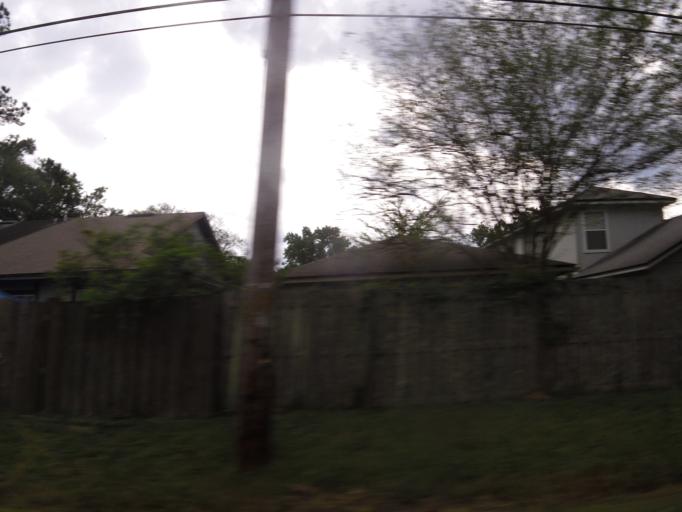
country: US
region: Florida
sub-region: Clay County
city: Orange Park
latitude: 30.1929
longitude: -81.7153
